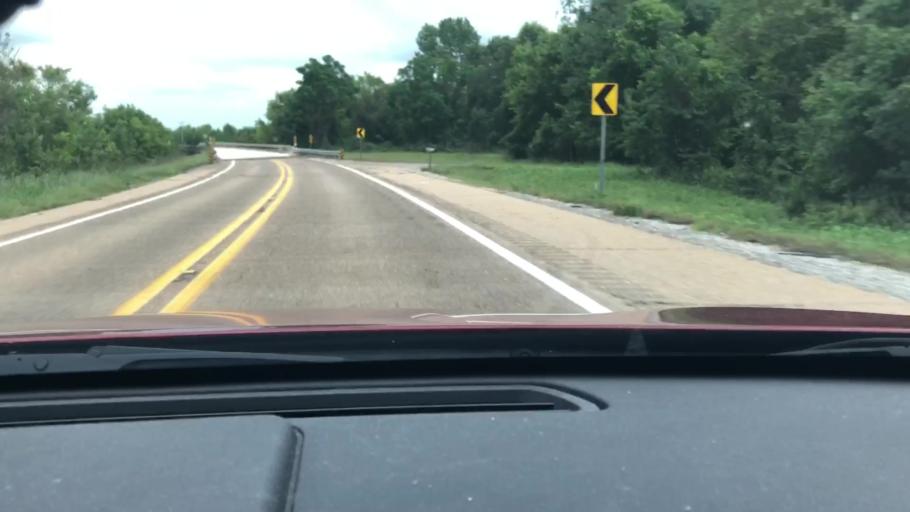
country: US
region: Arkansas
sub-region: Miller County
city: Texarkana
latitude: 33.4138
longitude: -93.8090
